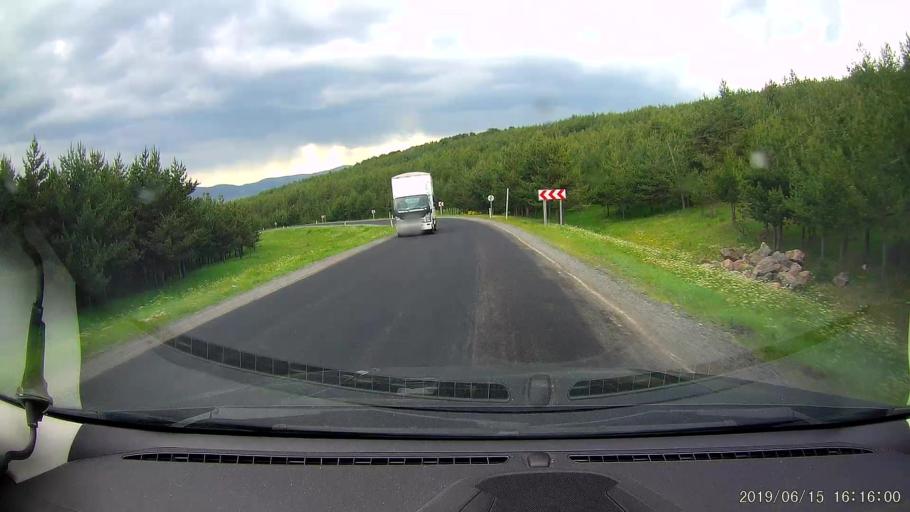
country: TR
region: Ardahan
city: Hanak
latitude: 41.2629
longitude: 42.8541
